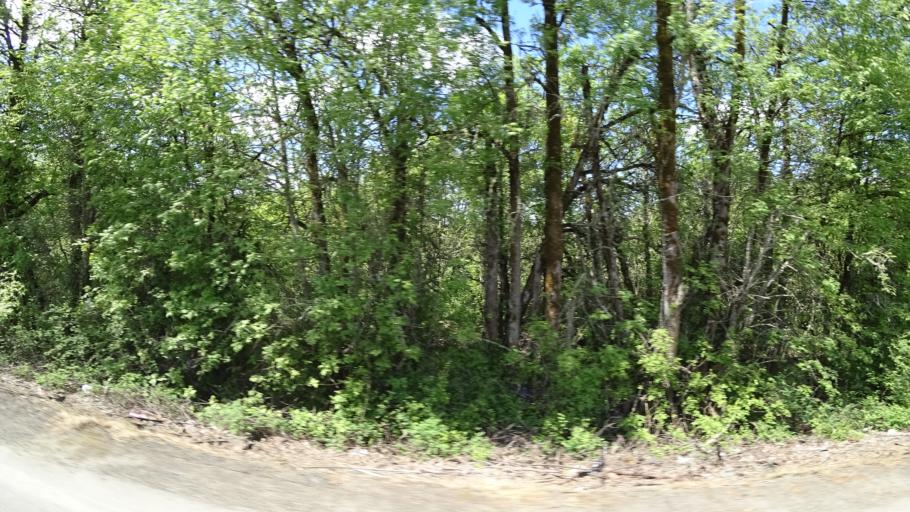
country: US
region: Oregon
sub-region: Washington County
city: Hillsboro
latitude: 45.5090
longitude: -122.9910
